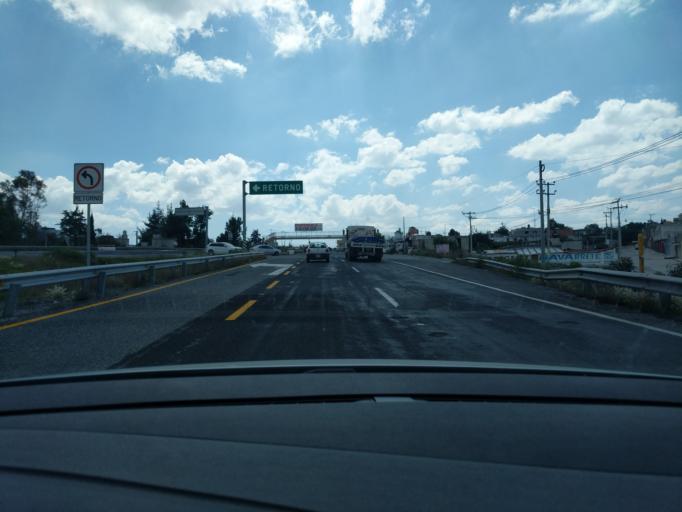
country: MX
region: Hidalgo
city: Zempoala
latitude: 19.9205
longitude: -98.6798
